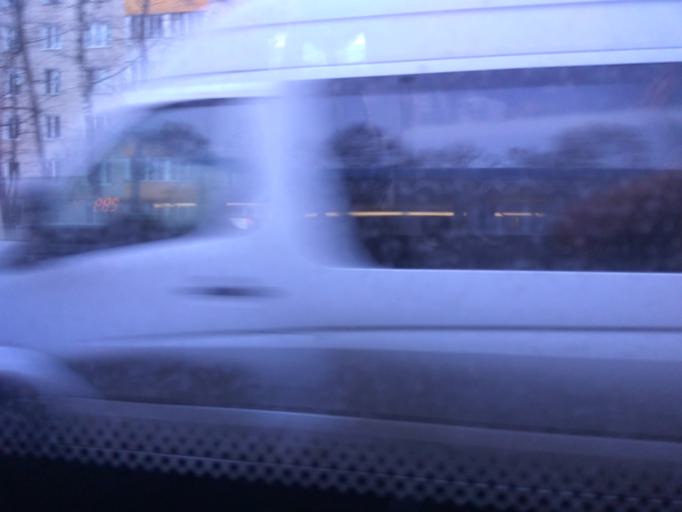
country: RU
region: Moscow
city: Biryulevo
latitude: 55.5935
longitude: 37.6635
